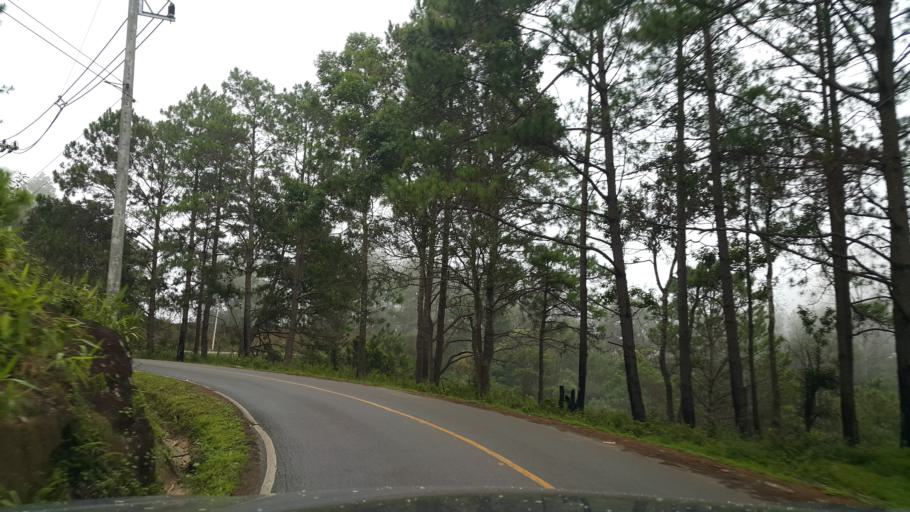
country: TH
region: Chiang Mai
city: Samoeng
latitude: 18.8811
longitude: 98.5242
